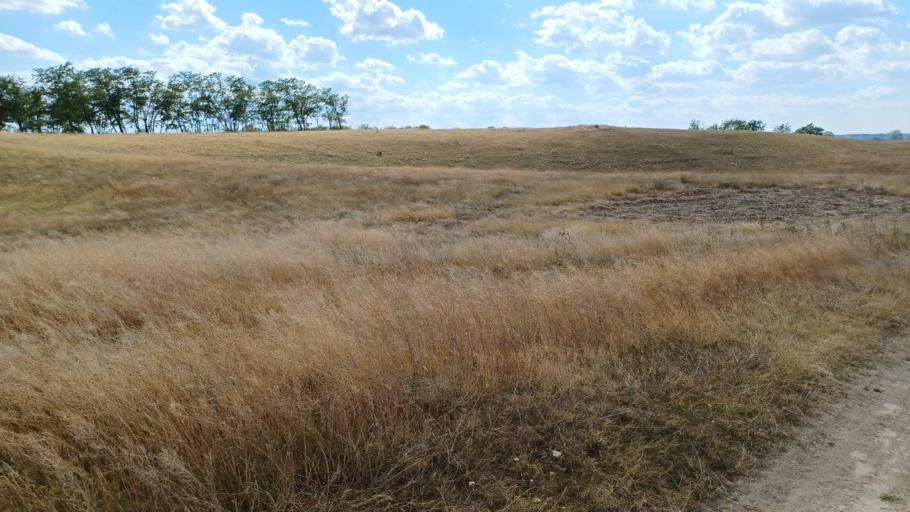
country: HU
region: Tolna
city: Tengelic
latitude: 46.5518
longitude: 18.6672
